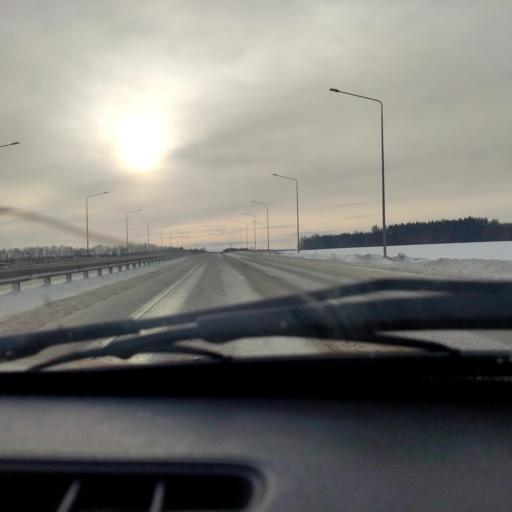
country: RU
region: Bashkortostan
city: Kabakovo
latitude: 54.4688
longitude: 55.9124
